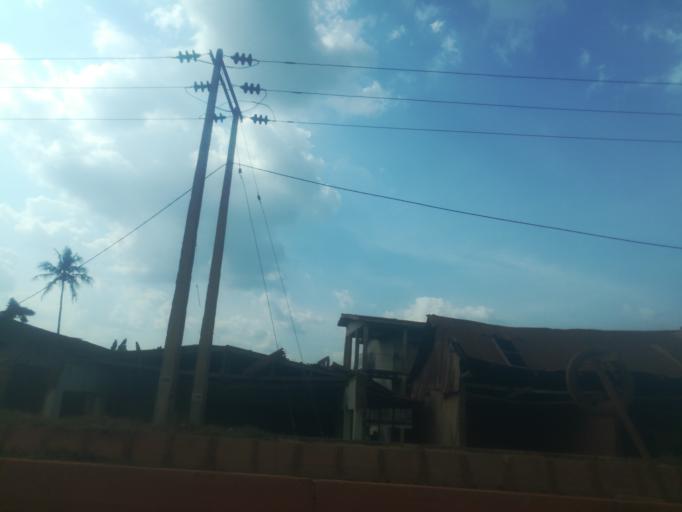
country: NG
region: Ogun
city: Abeokuta
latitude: 7.1685
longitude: 3.3368
